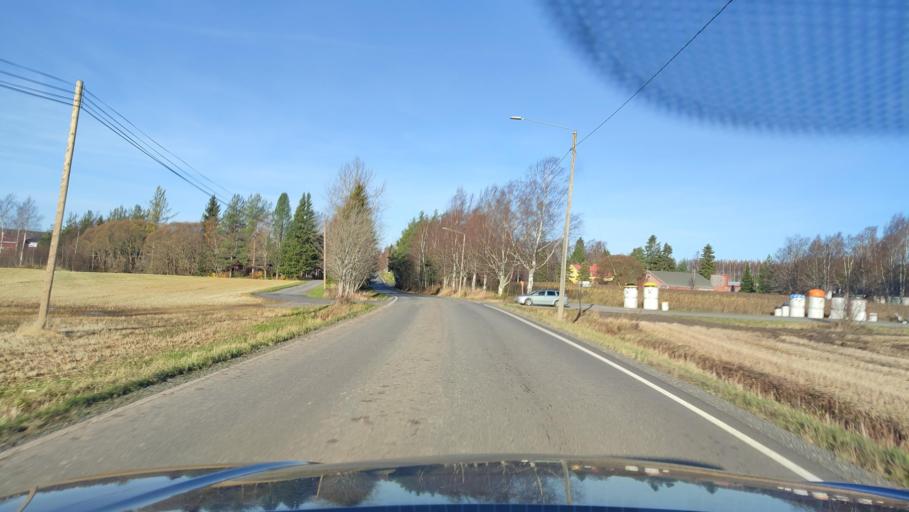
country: FI
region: Southern Ostrobothnia
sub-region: Suupohja
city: Karijoki
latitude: 62.3000
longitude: 21.7186
